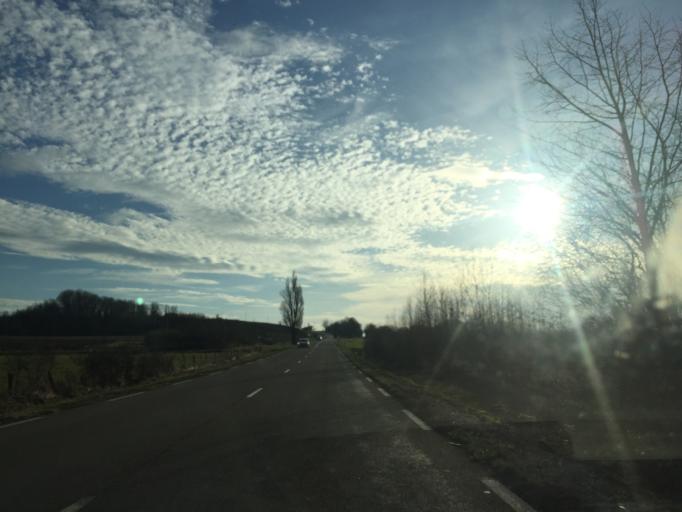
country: FR
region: Franche-Comte
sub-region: Departement du Jura
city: Arbois
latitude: 46.9377
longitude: 5.7777
